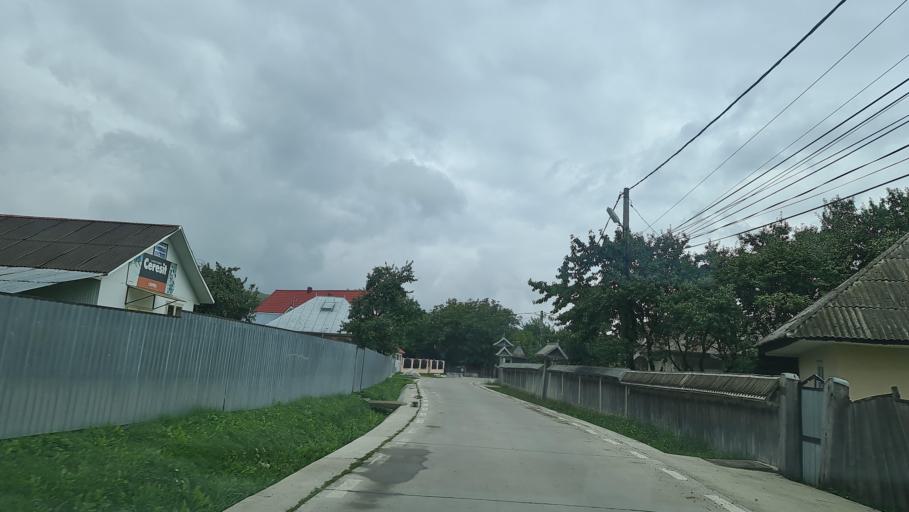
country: RO
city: Vanatori-Neamt
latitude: 47.2085
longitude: 26.3174
